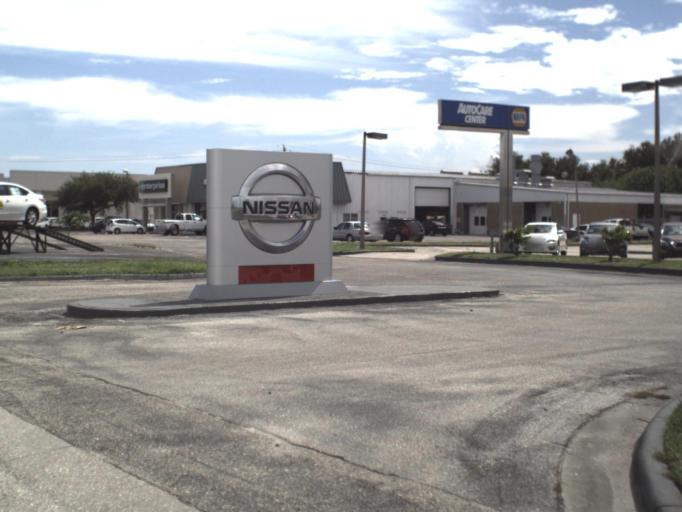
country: US
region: Florida
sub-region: Sarasota County
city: Venice
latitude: 27.0906
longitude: -82.4325
